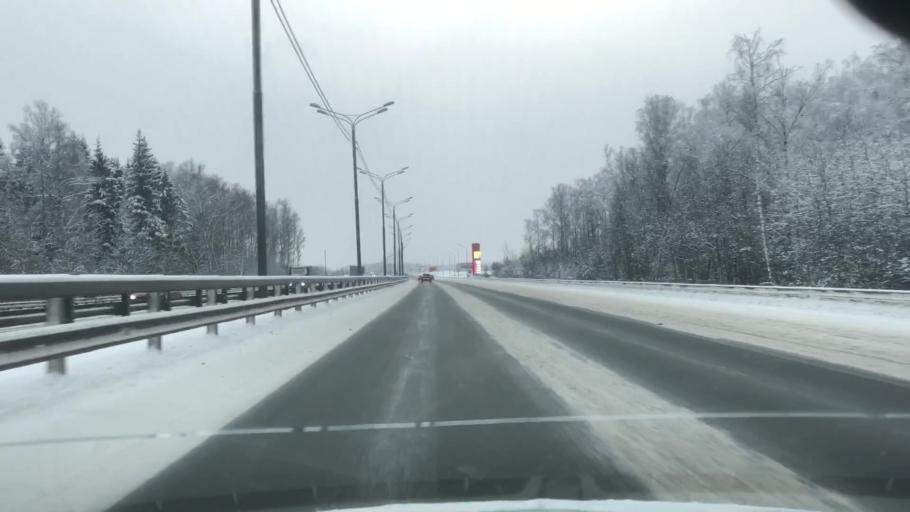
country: RU
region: Moskovskaya
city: Barybino
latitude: 55.1990
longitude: 37.8890
